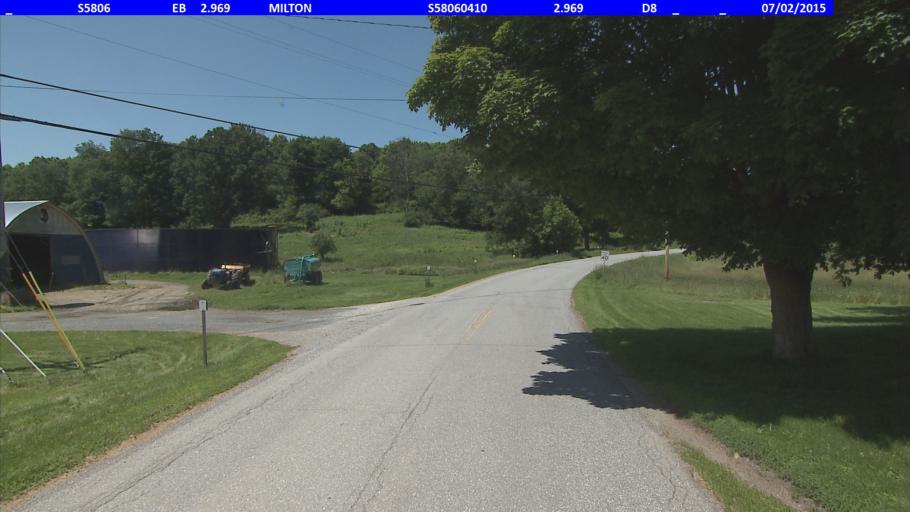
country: US
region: Vermont
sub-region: Chittenden County
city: Milton
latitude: 44.6679
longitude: -73.1667
